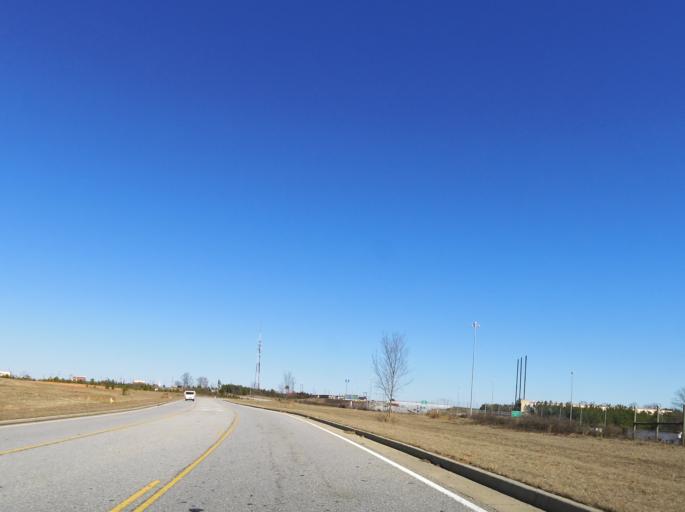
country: US
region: Georgia
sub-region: Peach County
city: Byron
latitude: 32.7364
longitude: -83.7238
